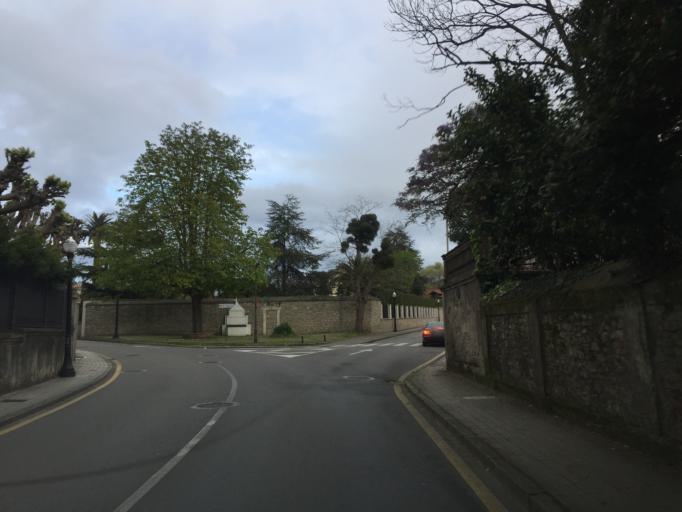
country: ES
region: Asturias
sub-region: Province of Asturias
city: Gijon
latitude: 43.5339
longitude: -5.6245
